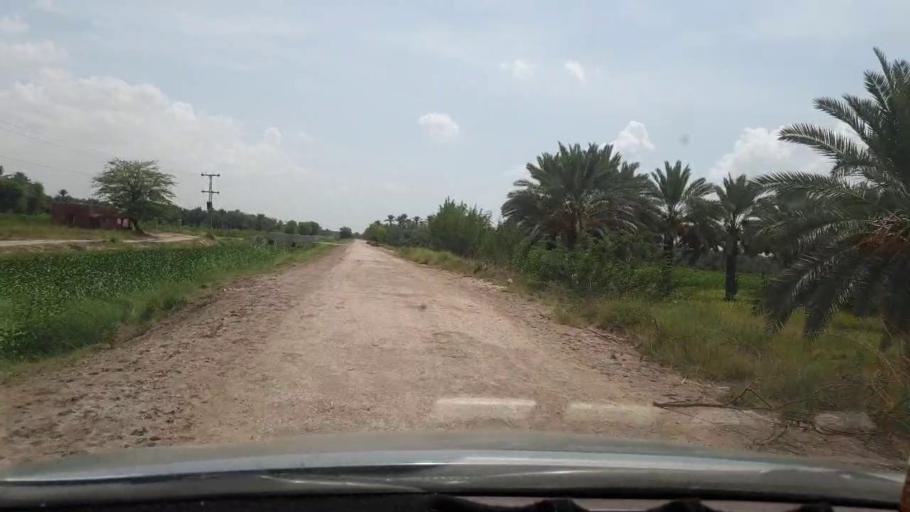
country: PK
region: Sindh
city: Khairpur
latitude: 27.4613
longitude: 68.7929
